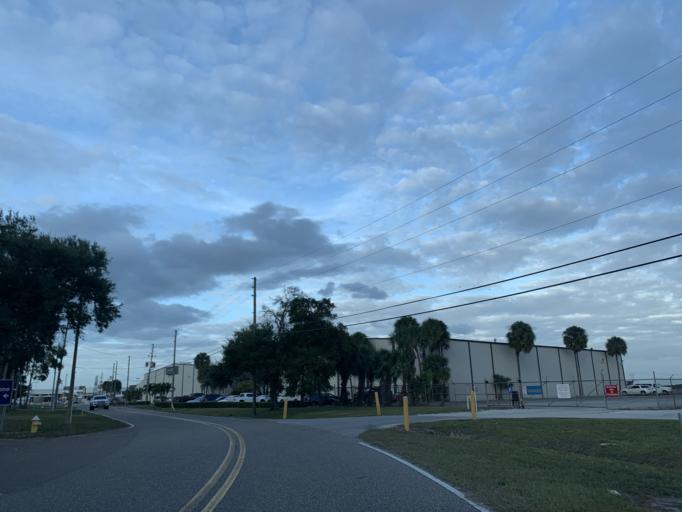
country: US
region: Florida
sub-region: Pinellas County
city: South Highpoint
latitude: 27.9031
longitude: -82.6913
